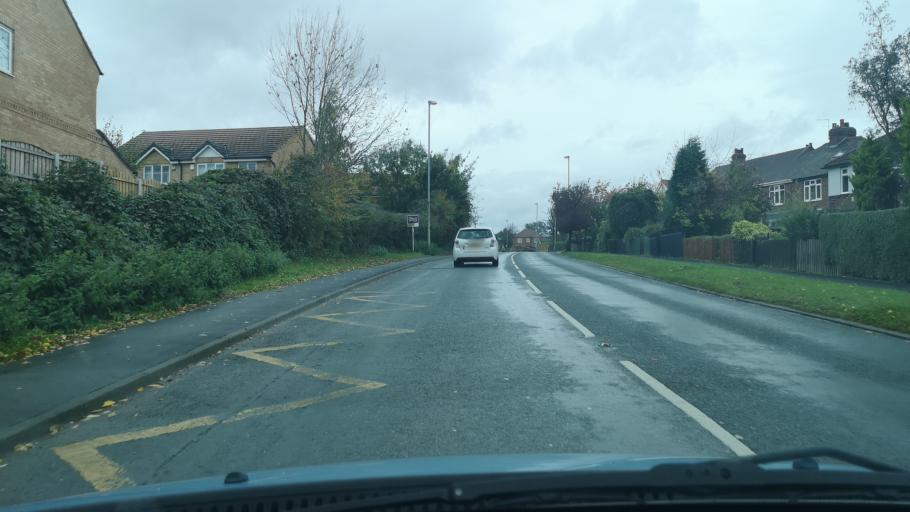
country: GB
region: England
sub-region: City and Borough of Wakefield
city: Low Ackworth
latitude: 53.6380
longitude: -1.3350
